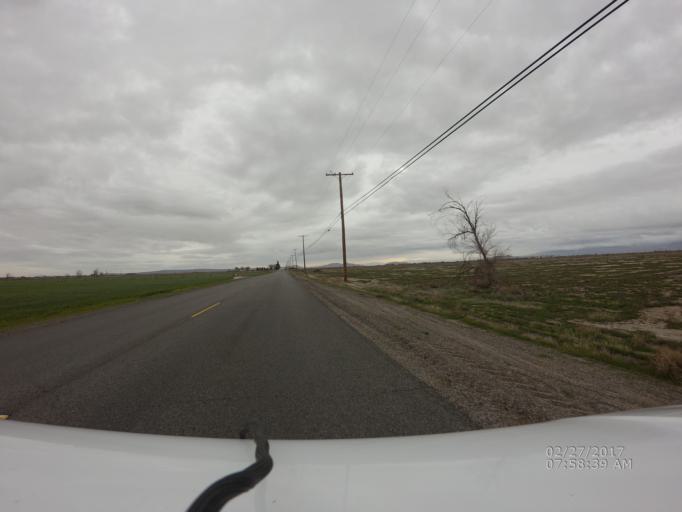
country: US
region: California
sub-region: Los Angeles County
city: Lancaster
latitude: 34.7047
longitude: -117.9948
